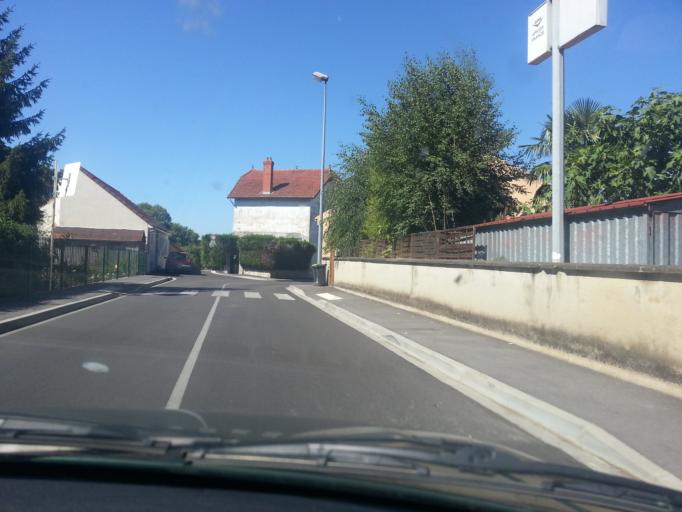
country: FR
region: Bourgogne
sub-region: Departement de Saone-et-Loire
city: Chalon-sur-Saone
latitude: 46.7812
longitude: 4.8676
